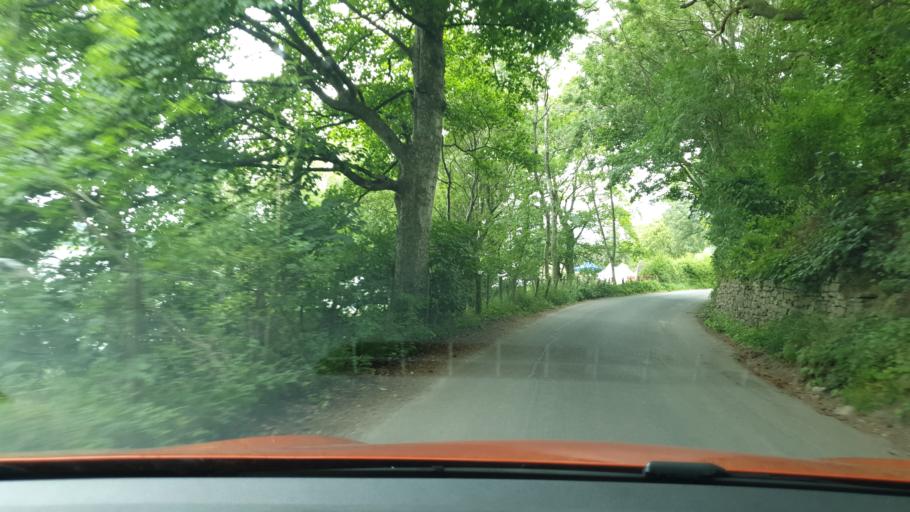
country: GB
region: England
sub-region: Cumbria
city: Penrith
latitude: 54.5984
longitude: -2.8354
